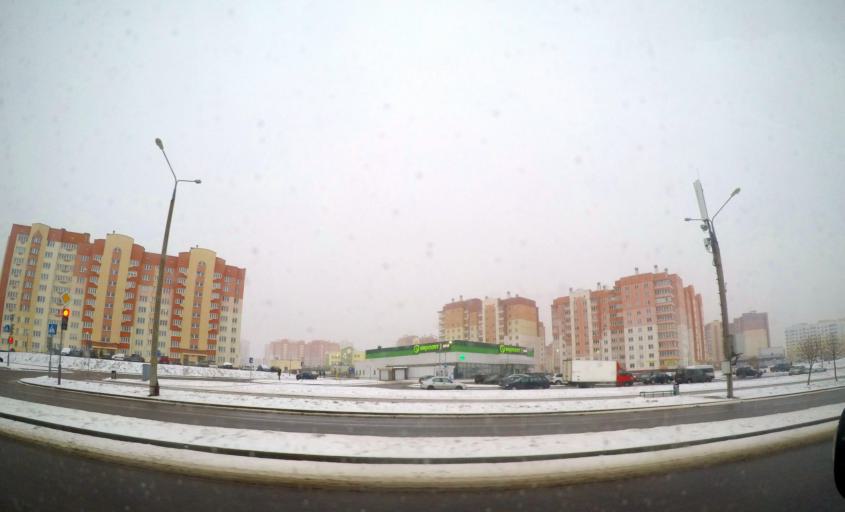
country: BY
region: Grodnenskaya
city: Hrodna
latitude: 53.6231
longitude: 23.8168
